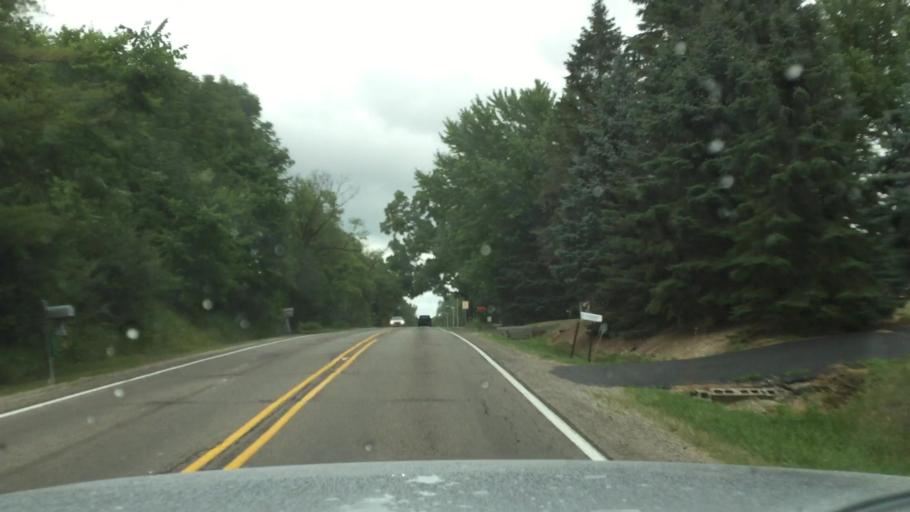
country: US
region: Michigan
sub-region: Genesee County
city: Clio
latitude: 43.1567
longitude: -83.7740
